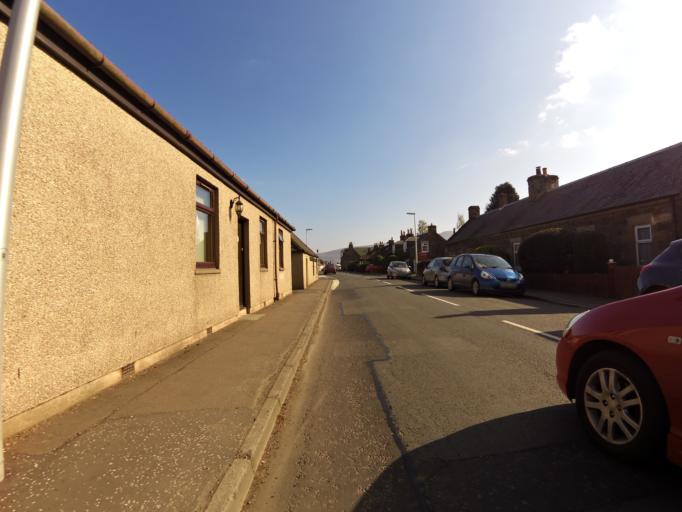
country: GB
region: Scotland
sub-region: Fife
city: Auchtermuchty
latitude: 56.2807
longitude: -3.2145
